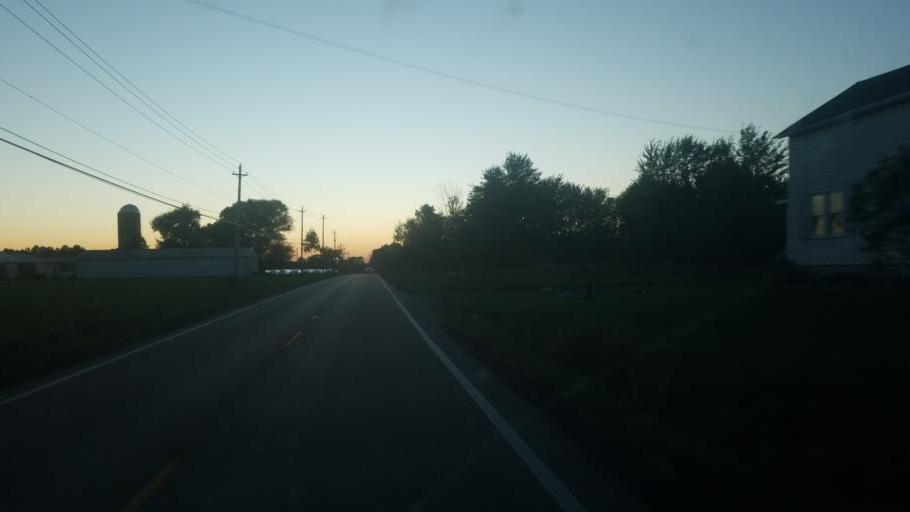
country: US
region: Ohio
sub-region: Ashtabula County
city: Andover
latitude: 41.7514
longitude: -80.5905
